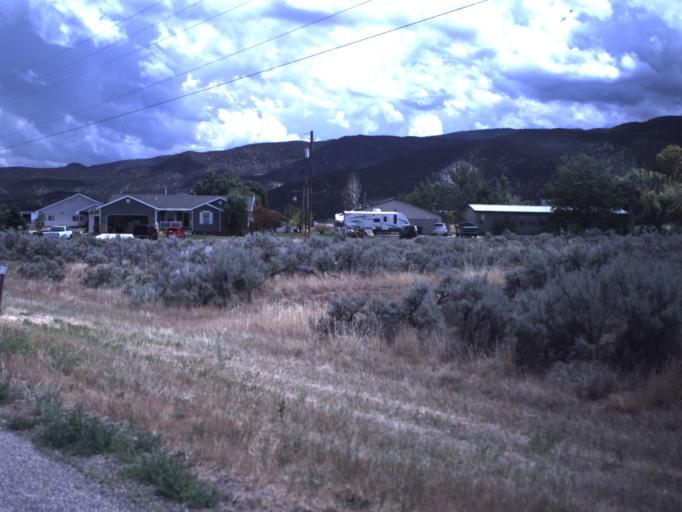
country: US
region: Utah
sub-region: Iron County
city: Parowan
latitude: 37.8527
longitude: -112.8248
